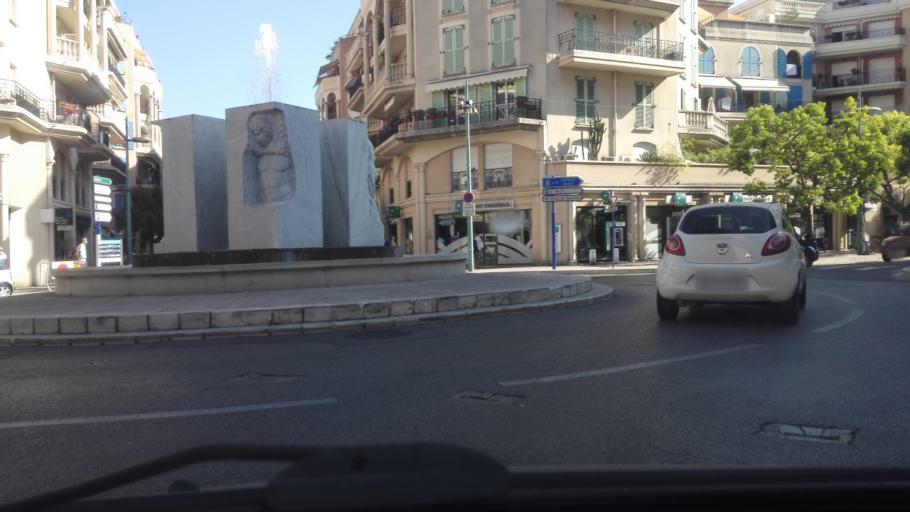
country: FR
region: Provence-Alpes-Cote d'Azur
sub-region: Departement des Alpes-Maritimes
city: Menton
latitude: 43.7745
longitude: 7.5012
